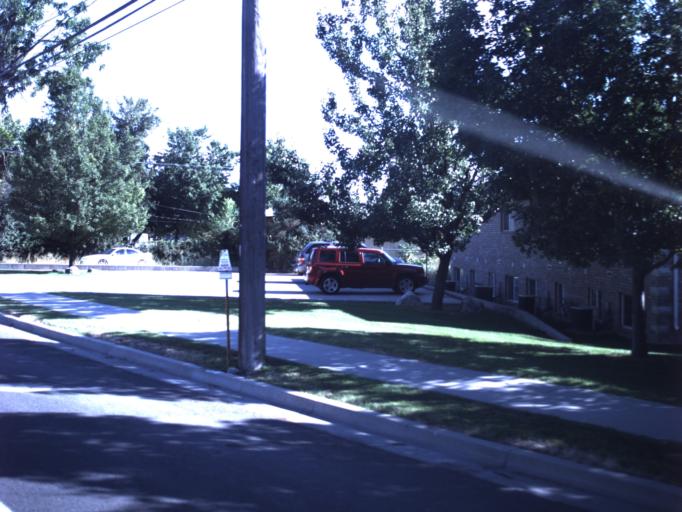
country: US
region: Utah
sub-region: Utah County
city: Provo
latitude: 40.2220
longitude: -111.6408
